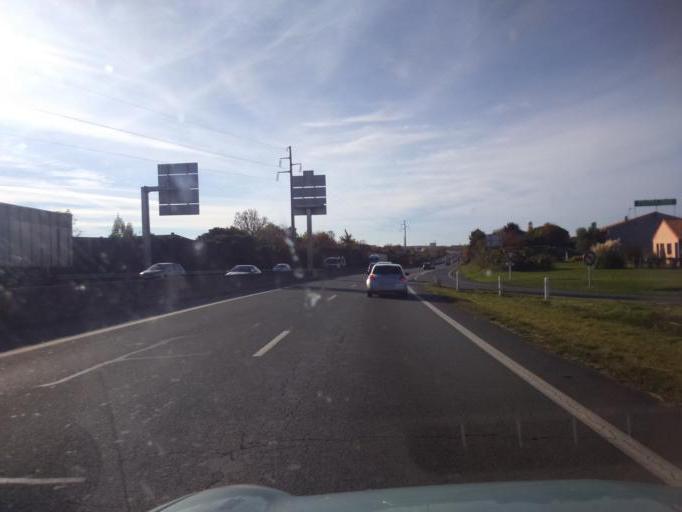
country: FR
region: Poitou-Charentes
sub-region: Departement de la Charente-Maritime
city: Puilboreau
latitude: 46.1703
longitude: -1.1206
